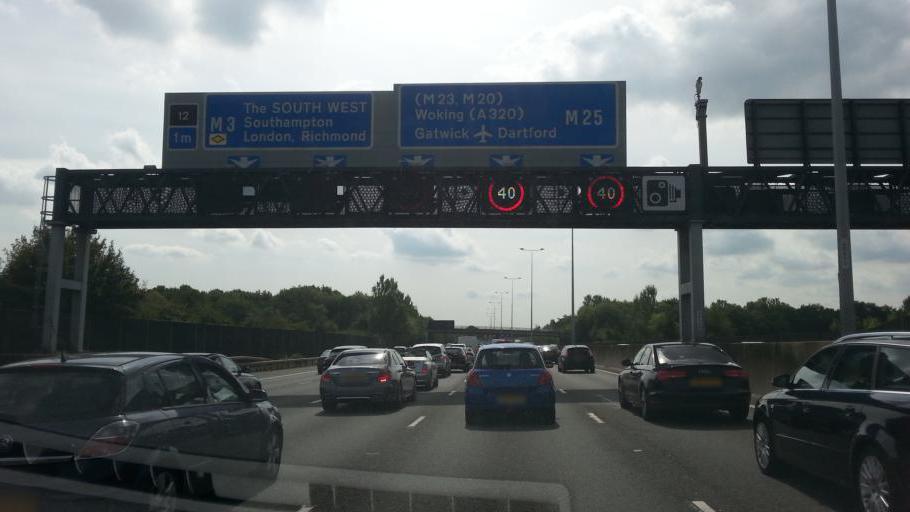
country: GB
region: England
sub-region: Surrey
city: Egham
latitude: 51.4261
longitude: -0.5407
